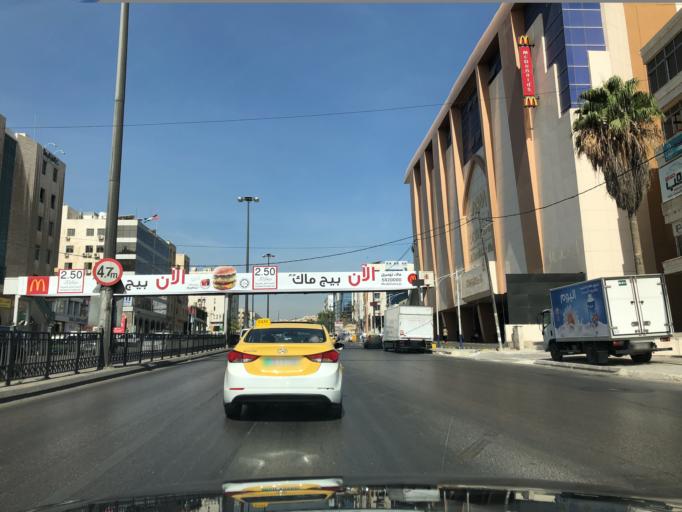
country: JO
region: Amman
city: Al Jubayhah
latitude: 31.9869
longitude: 35.8968
